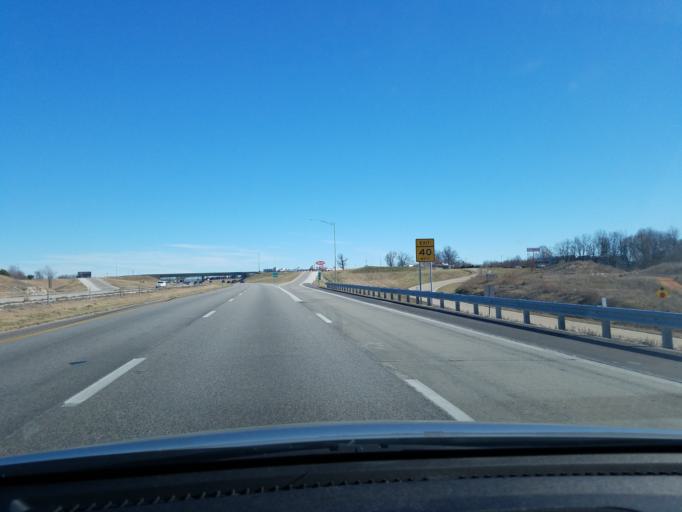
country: US
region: Missouri
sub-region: Greene County
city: Strafford
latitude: 37.2501
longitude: -93.1879
